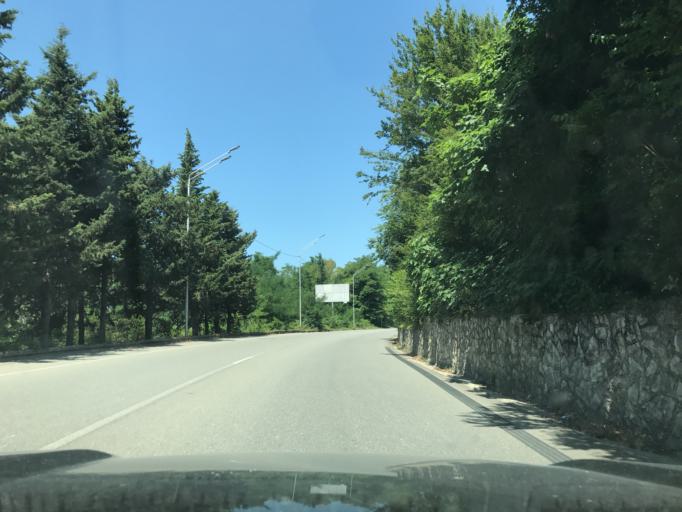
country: GE
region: Abkhazia
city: Gagra
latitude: 43.2815
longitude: 40.2763
